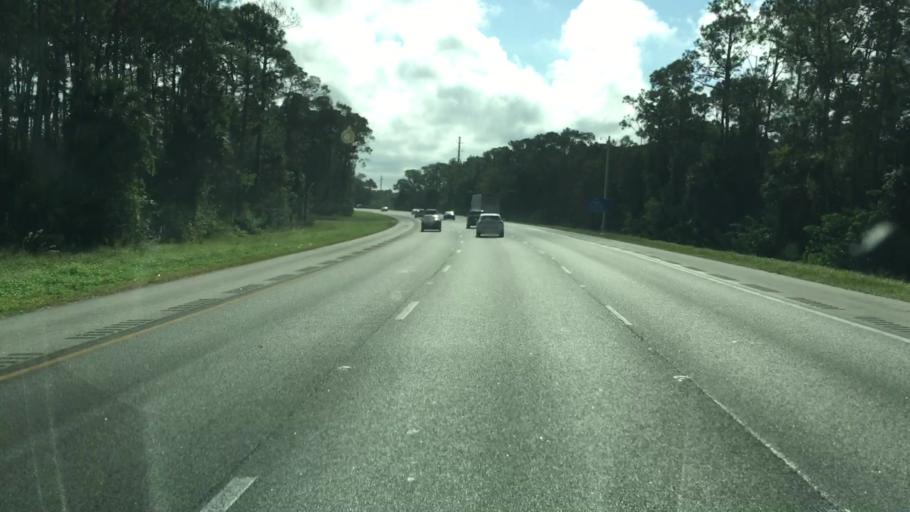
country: US
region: Florida
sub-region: Volusia County
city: Port Orange
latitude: 29.1312
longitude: -81.0618
